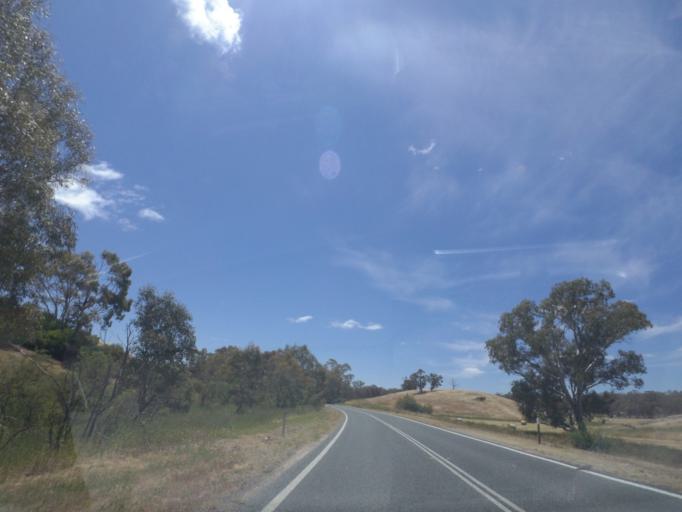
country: AU
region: Victoria
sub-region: Mount Alexander
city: Castlemaine
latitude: -37.1910
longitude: 144.1491
